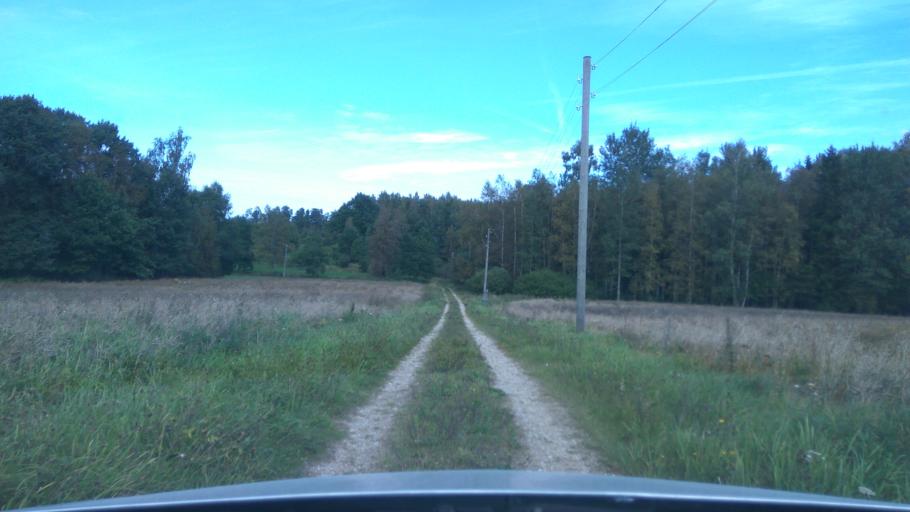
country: LV
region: Kuldigas Rajons
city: Kuldiga
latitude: 57.2395
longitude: 21.9630
